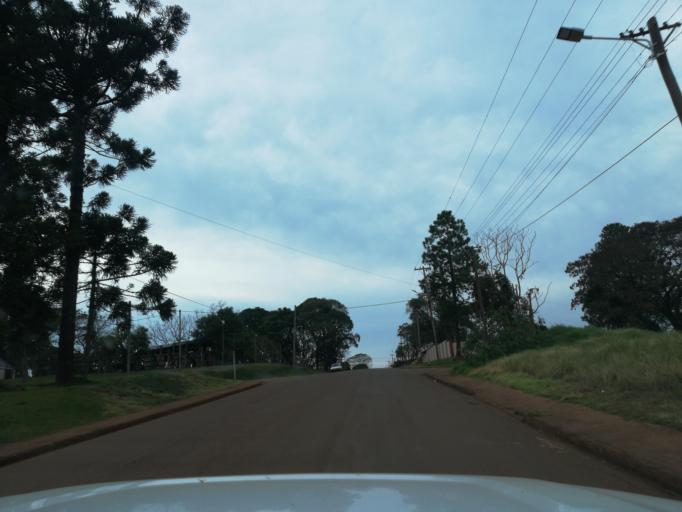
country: AR
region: Misiones
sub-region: Departamento de San Pedro
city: San Pedro
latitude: -26.6240
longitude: -54.1045
